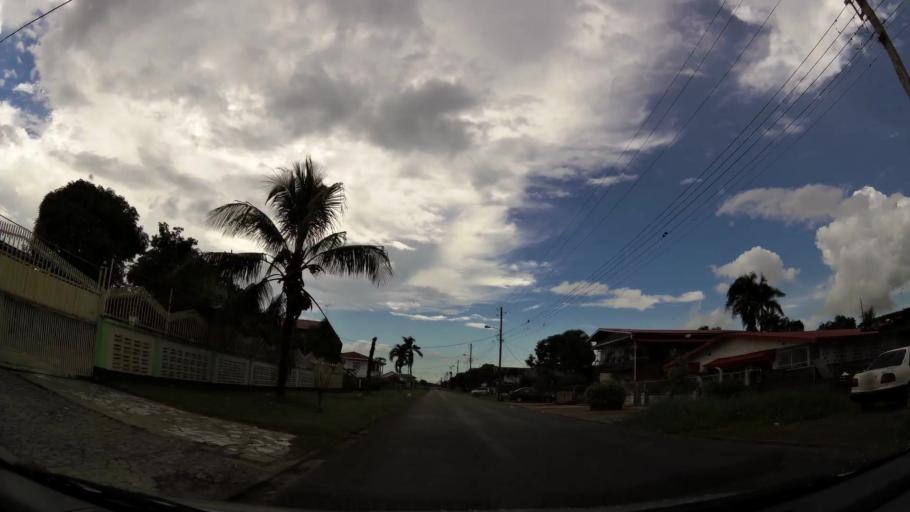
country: SR
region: Paramaribo
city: Paramaribo
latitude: 5.8447
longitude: -55.1274
